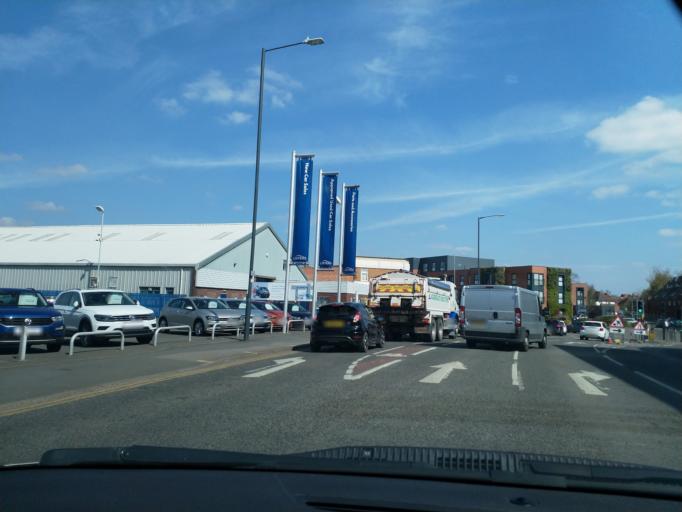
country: GB
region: England
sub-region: Warwickshire
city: Stratford-upon-Avon
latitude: 52.1955
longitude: -1.7112
